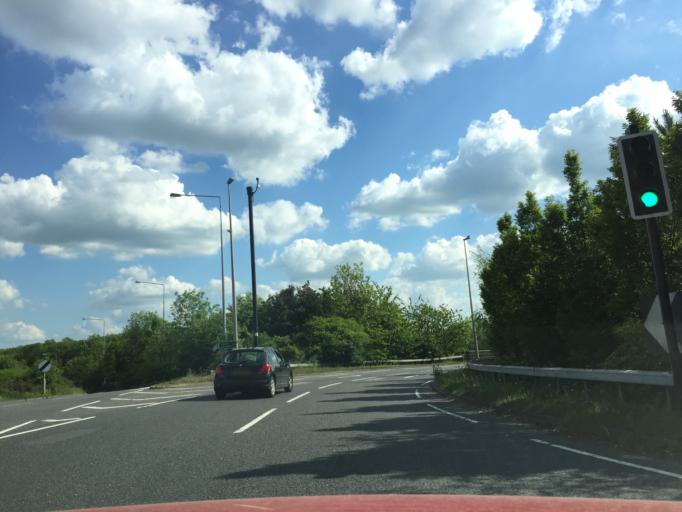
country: GB
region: England
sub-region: Milton Keynes
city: Loughton
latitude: 52.0376
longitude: -0.7809
